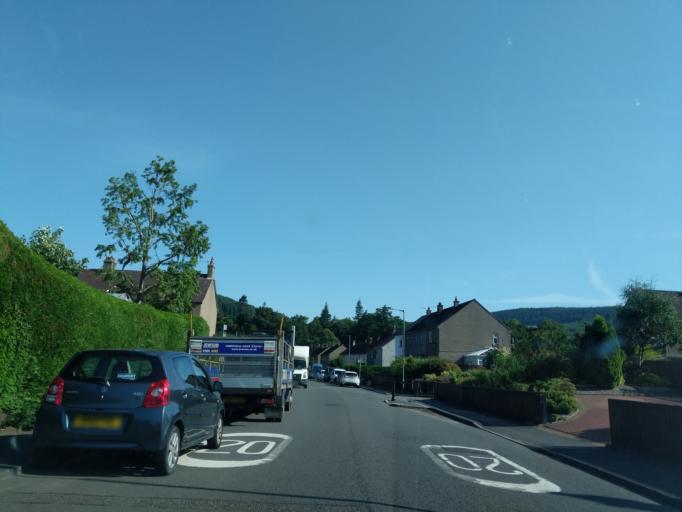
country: GB
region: Scotland
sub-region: The Scottish Borders
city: Peebles
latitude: 55.6458
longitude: -3.1830
